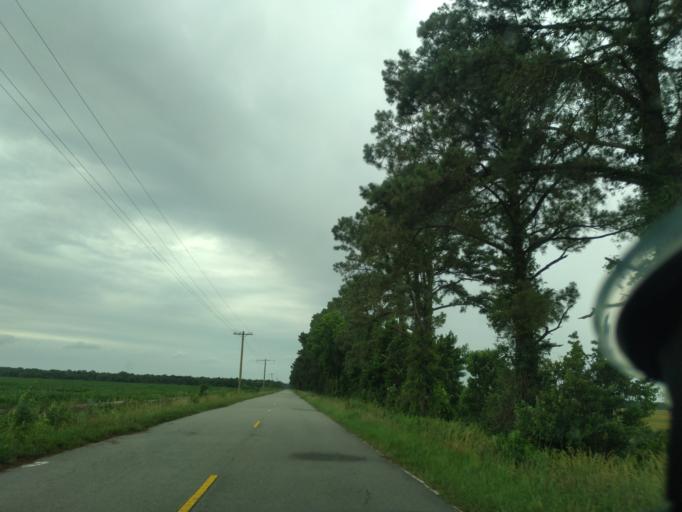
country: US
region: North Carolina
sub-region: Washington County
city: Plymouth
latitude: 35.8127
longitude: -76.5156
